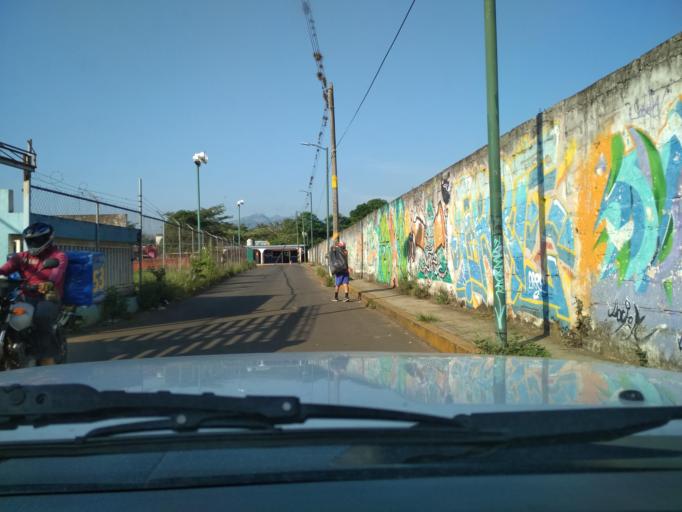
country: MX
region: Veracruz
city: Cordoba
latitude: 18.8721
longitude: -96.9326
